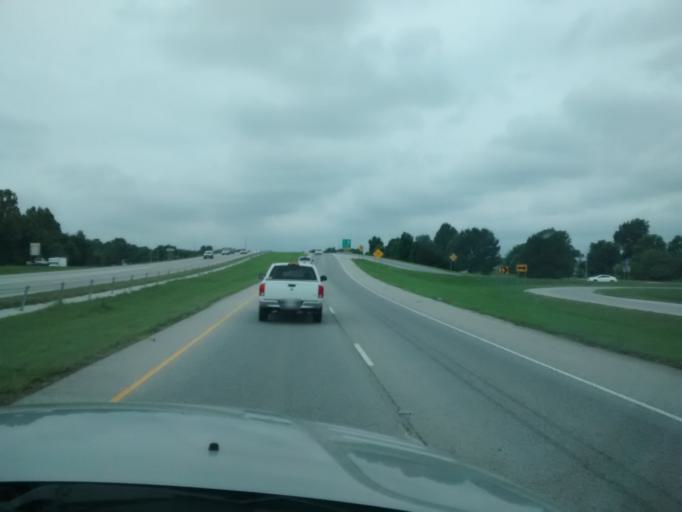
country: US
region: Arkansas
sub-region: Washington County
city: Johnson
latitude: 36.1129
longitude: -94.1594
